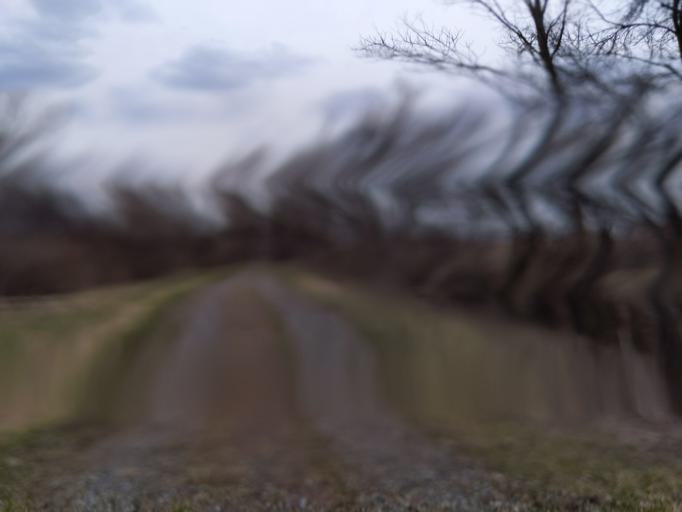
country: US
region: New York
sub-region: Tompkins County
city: Dryden
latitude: 42.5017
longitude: -76.3365
